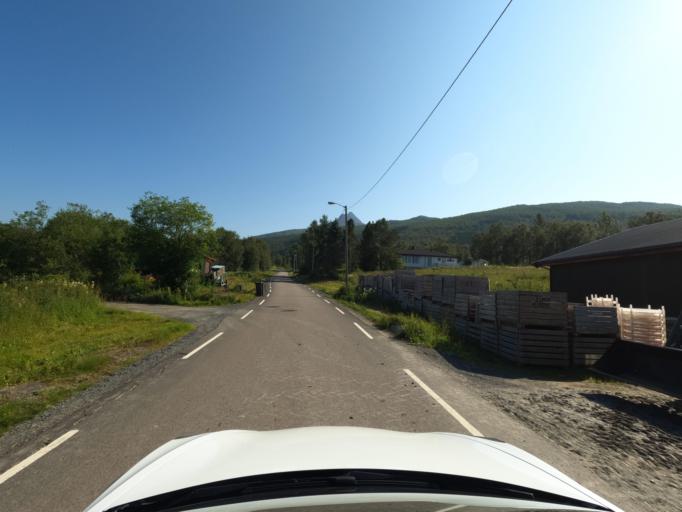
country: NO
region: Nordland
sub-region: Narvik
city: Narvik
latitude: 68.3994
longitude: 17.2942
